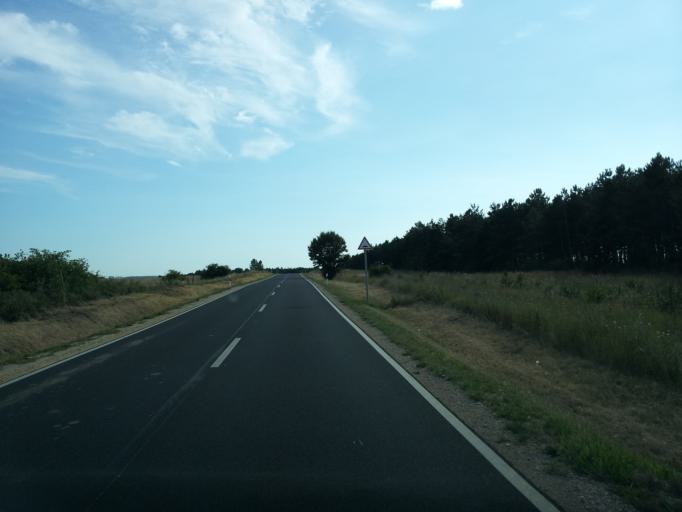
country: HU
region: Veszprem
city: Herend
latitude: 47.0101
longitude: 17.7549
